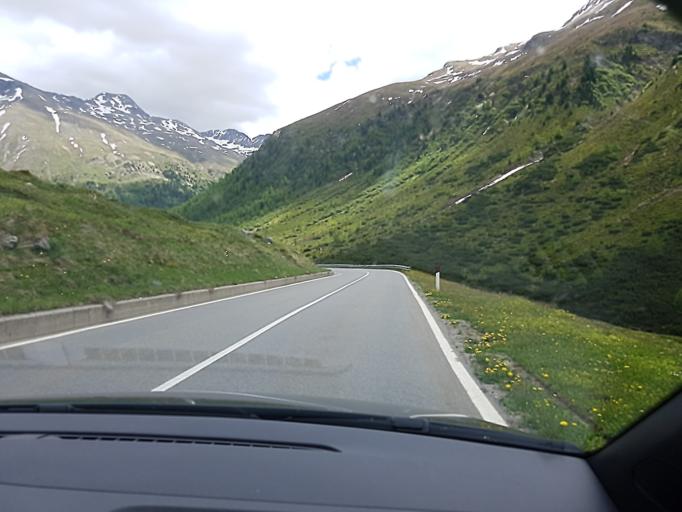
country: IT
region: Lombardy
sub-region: Provincia di Sondrio
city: Livigno
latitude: 46.4619
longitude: 10.0727
